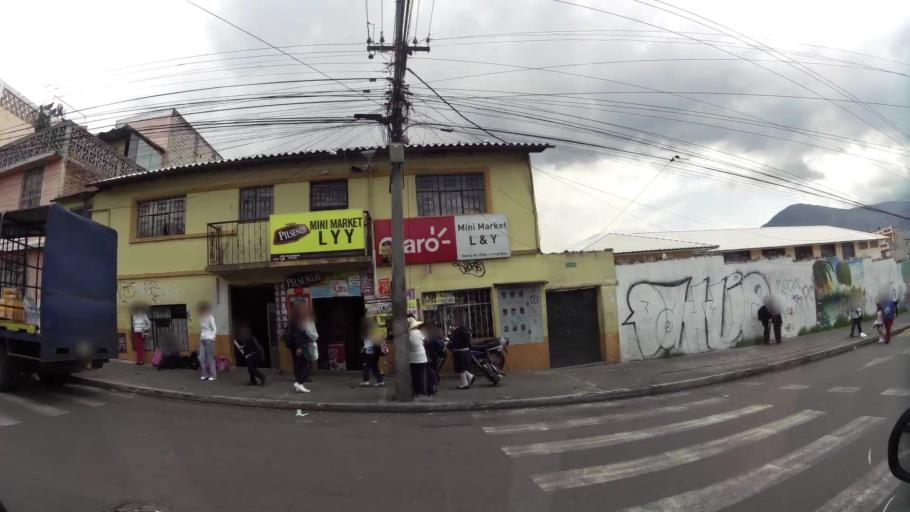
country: EC
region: Pichincha
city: Quito
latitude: -0.2547
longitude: -78.5153
